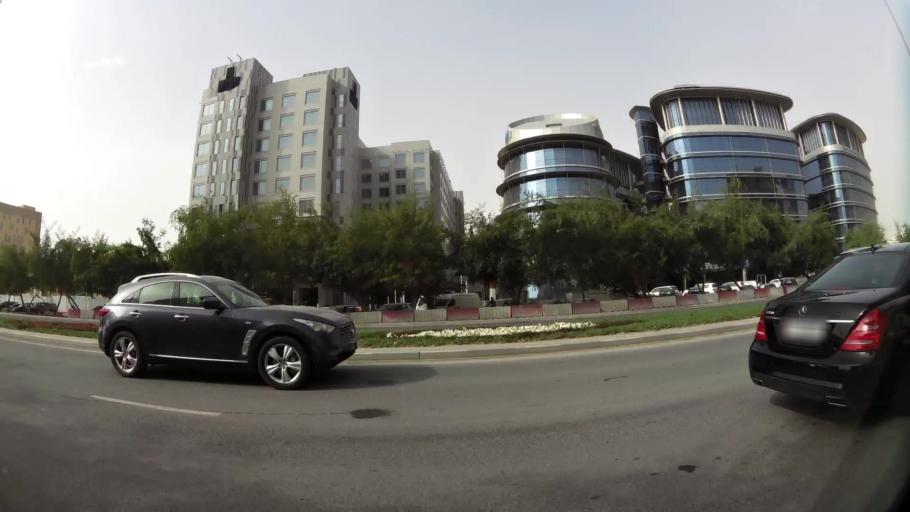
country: QA
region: Baladiyat ad Dawhah
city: Doha
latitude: 25.2738
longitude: 51.5426
